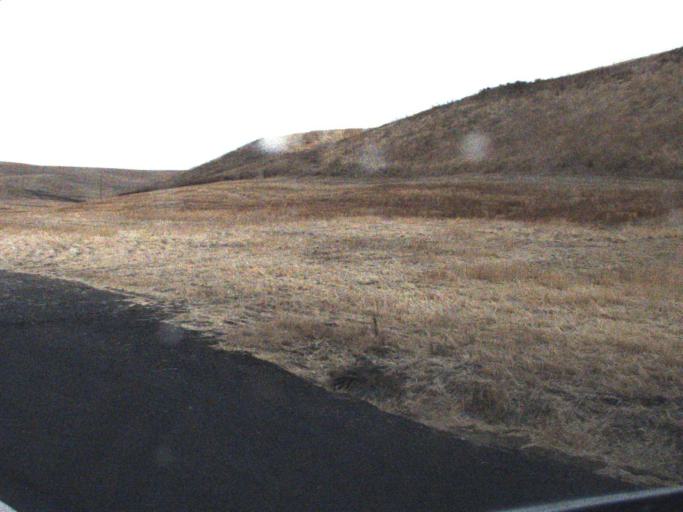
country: US
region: Washington
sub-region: Adams County
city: Ritzville
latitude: 46.7865
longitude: -118.3851
